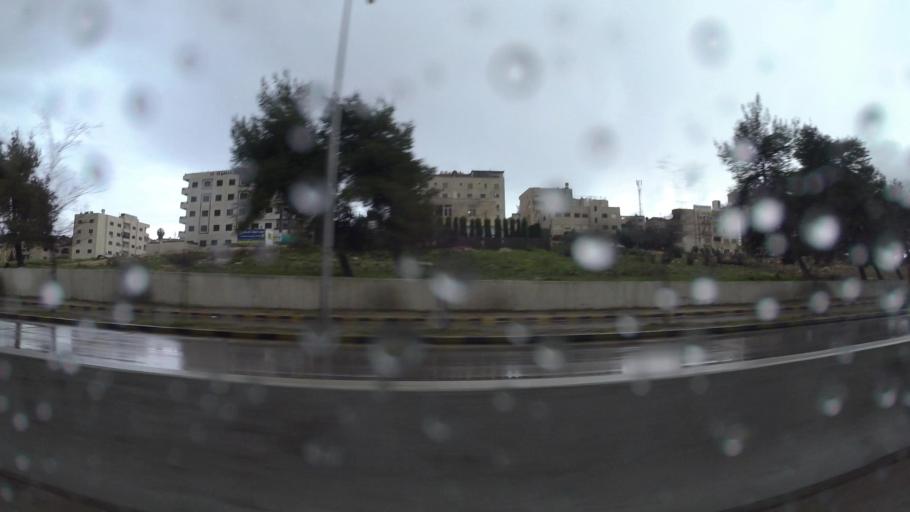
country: JO
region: Amman
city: Umm as Summaq
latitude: 31.8967
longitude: 35.8554
